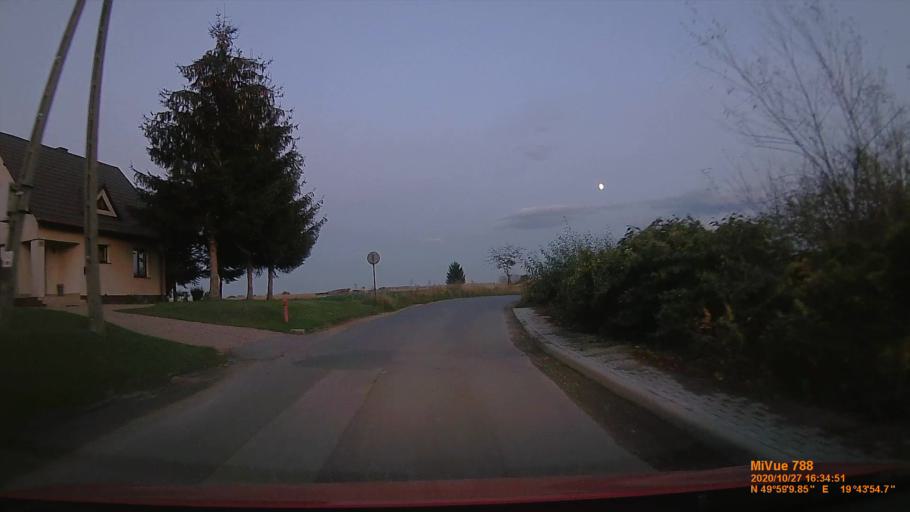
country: PL
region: Lesser Poland Voivodeship
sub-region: Powiat krakowski
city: Wolowice
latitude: 49.9861
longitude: 19.7319
